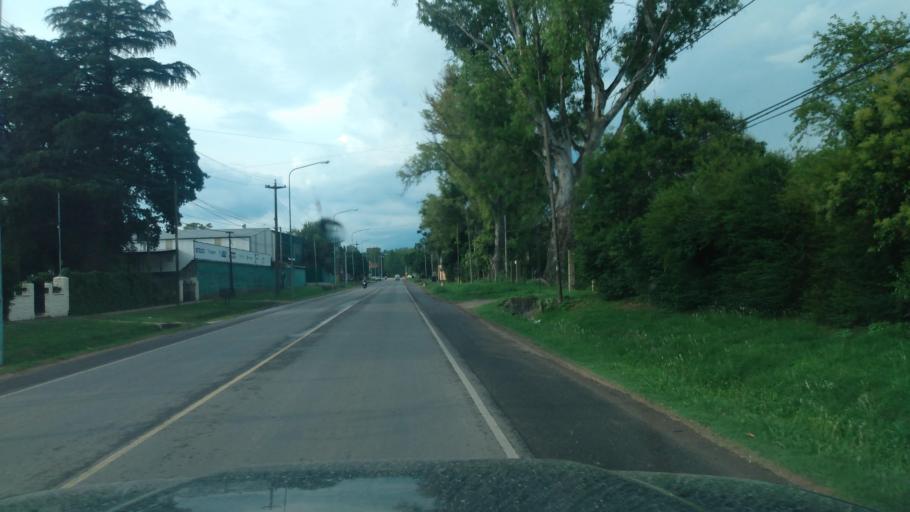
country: AR
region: Buenos Aires
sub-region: Partido de Lujan
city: Lujan
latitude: -34.5539
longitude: -59.1256
